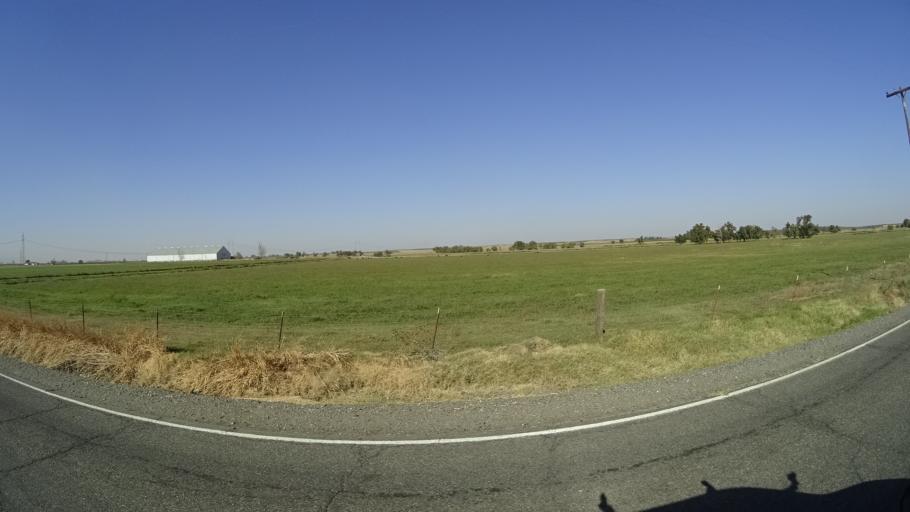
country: US
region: California
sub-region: Yolo County
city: Cottonwood
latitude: 38.7162
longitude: -121.9359
